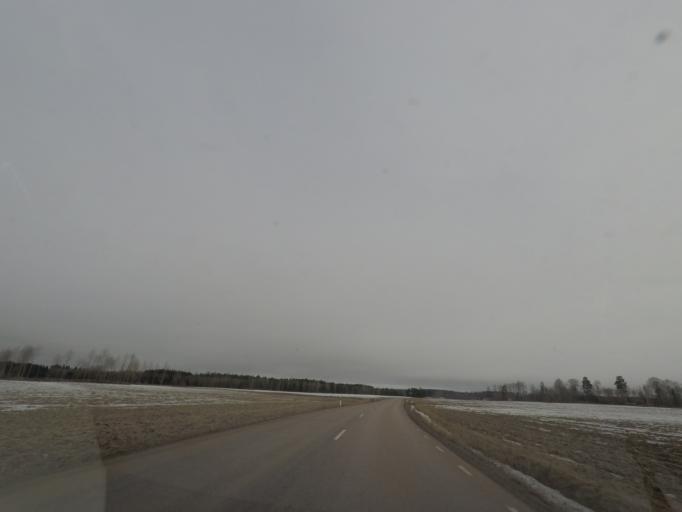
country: SE
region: Vaestmanland
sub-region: Vasteras
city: Skultuna
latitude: 59.7348
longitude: 16.4132
